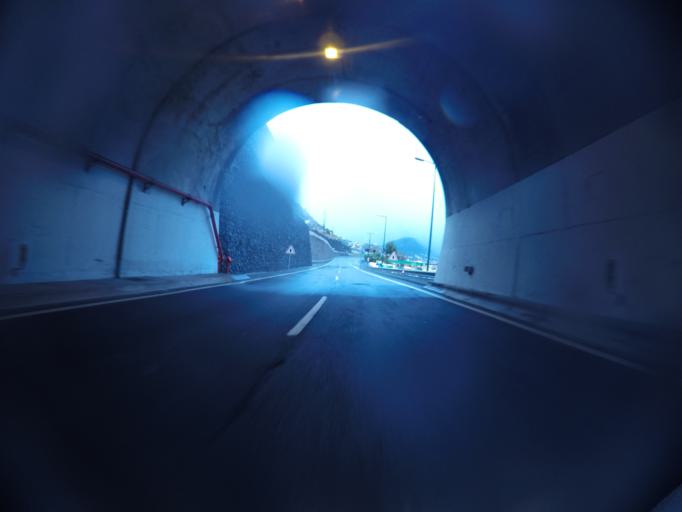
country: PT
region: Madeira
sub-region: Machico
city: Machico
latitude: 32.7126
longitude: -16.7657
